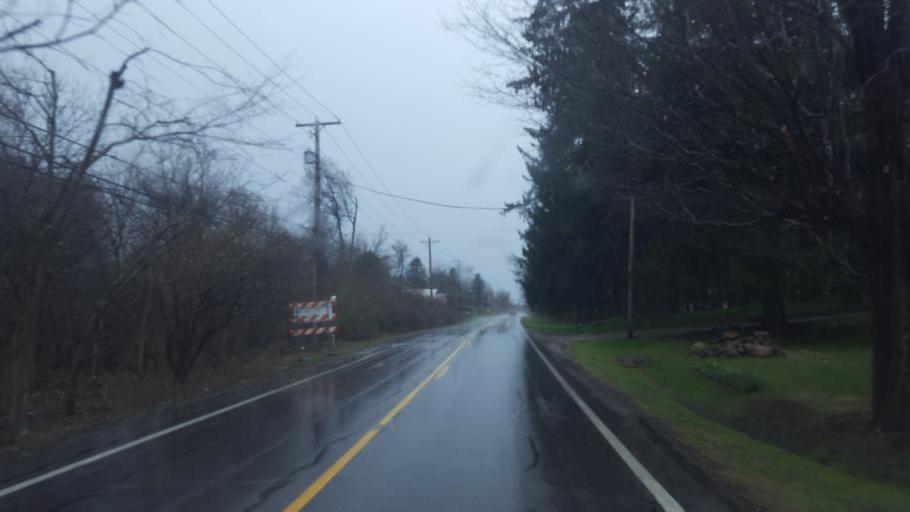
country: US
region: Ohio
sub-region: Delaware County
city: Powell
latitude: 40.1484
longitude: -83.0431
